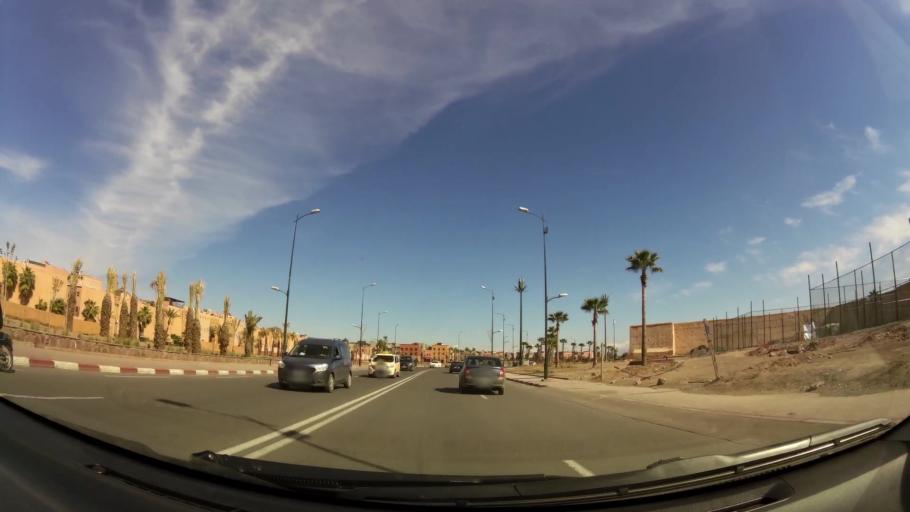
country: MA
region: Marrakech-Tensift-Al Haouz
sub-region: Marrakech
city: Marrakesh
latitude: 31.6393
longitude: -7.9820
